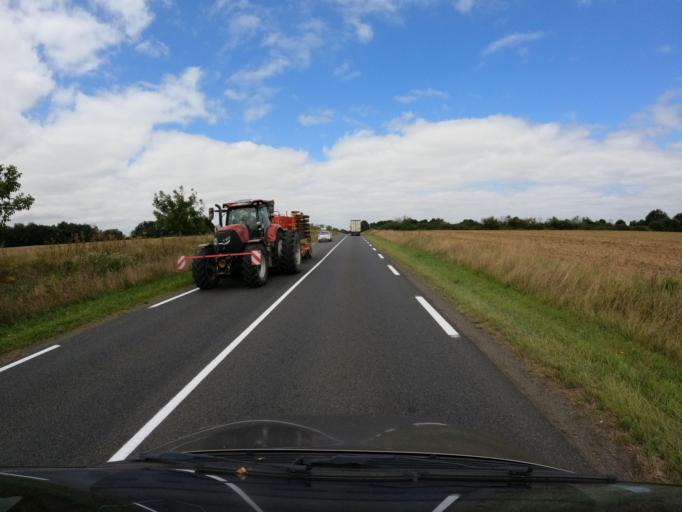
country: FR
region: Poitou-Charentes
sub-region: Departement de la Vienne
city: Charroux
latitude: 46.1439
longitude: 0.4172
